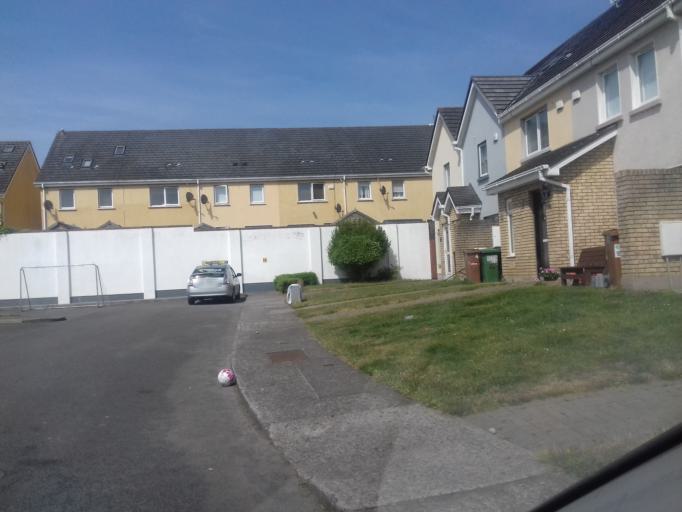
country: IE
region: Leinster
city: Lusk
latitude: 53.5223
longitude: -6.1691
